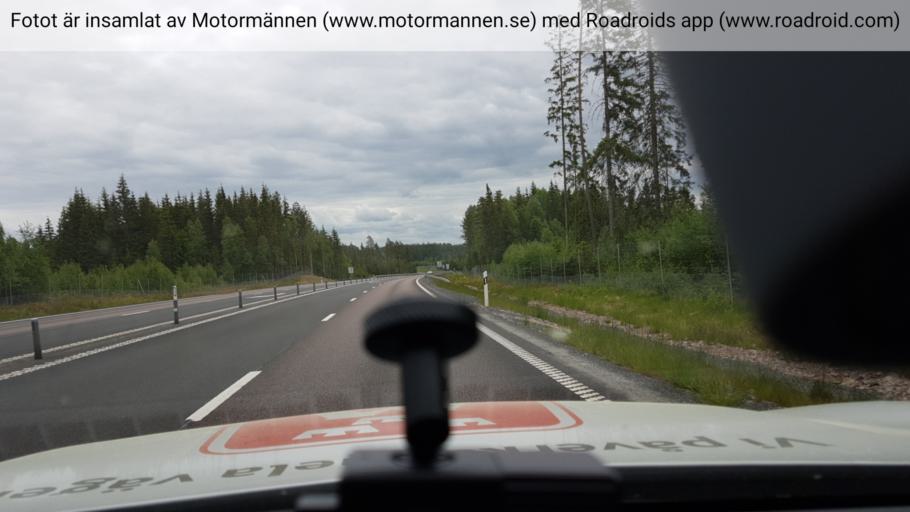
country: SE
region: Joenkoeping
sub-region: Mullsjo Kommun
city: Mullsjoe
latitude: 57.8931
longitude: 13.8842
